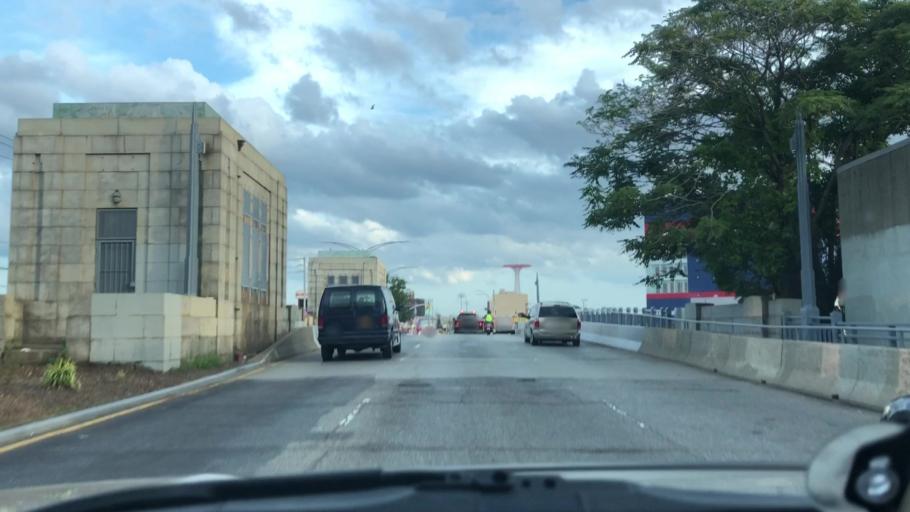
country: US
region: New York
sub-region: Kings County
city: Coney Island
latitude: 40.5820
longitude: -73.9861
